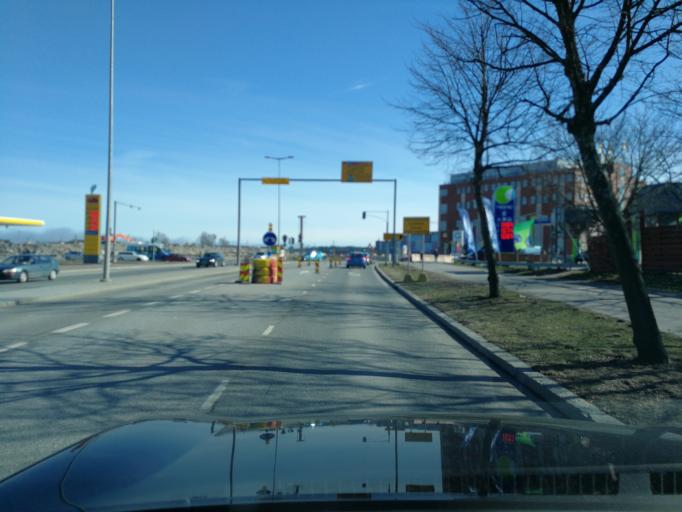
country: FI
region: Uusimaa
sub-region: Helsinki
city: Helsinki
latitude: 60.1935
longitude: 24.9774
